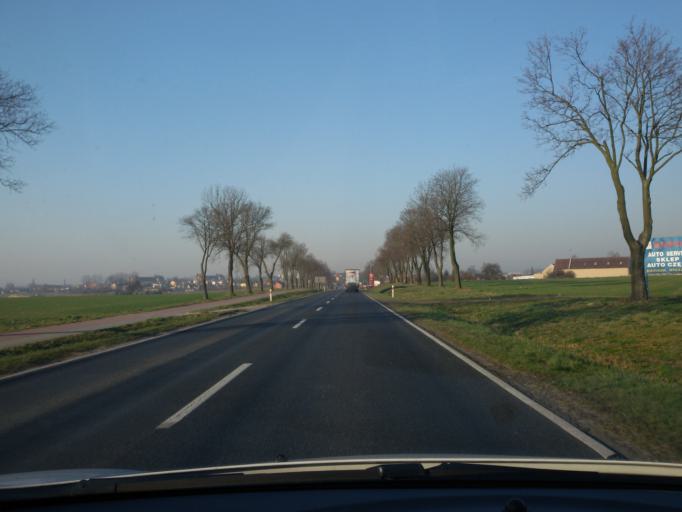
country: PL
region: Lubusz
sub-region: Powiat wschowski
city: Wschowa
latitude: 51.8149
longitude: 16.3382
